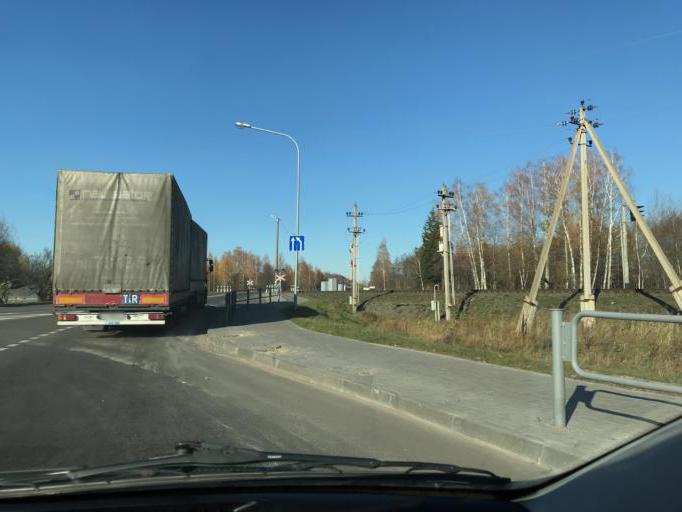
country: BY
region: Vitebsk
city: Polatsk
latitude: 55.5049
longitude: 28.7486
